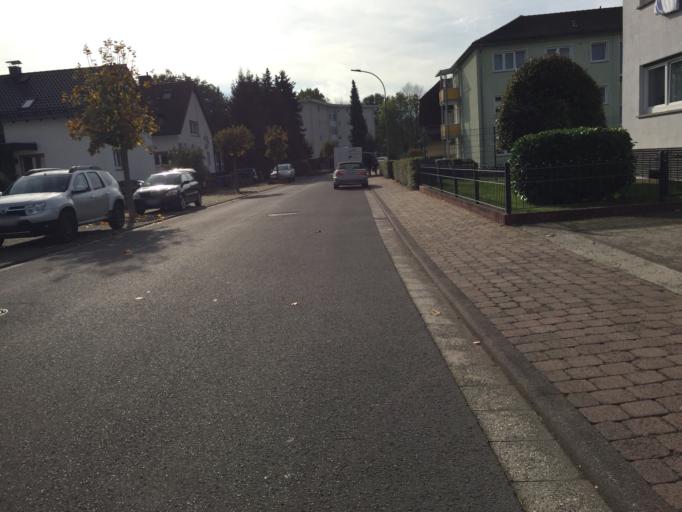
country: DE
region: Hesse
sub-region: Regierungsbezirk Giessen
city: Laubach
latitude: 50.5436
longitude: 8.9823
